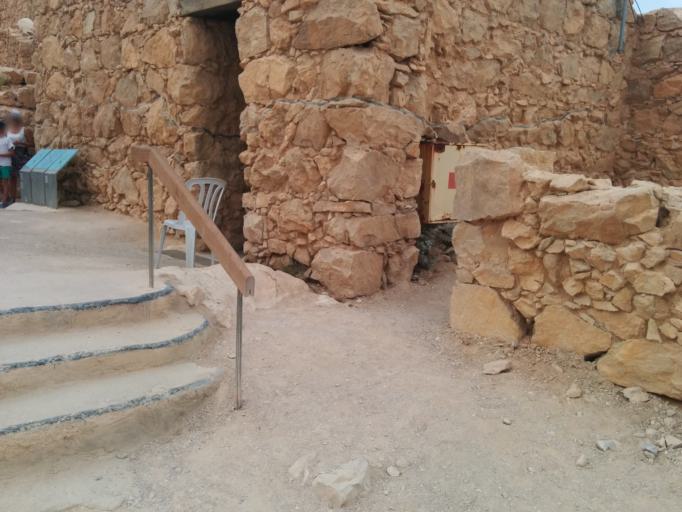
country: IL
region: Southern District
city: `En Boqeq
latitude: 31.3165
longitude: 35.3548
